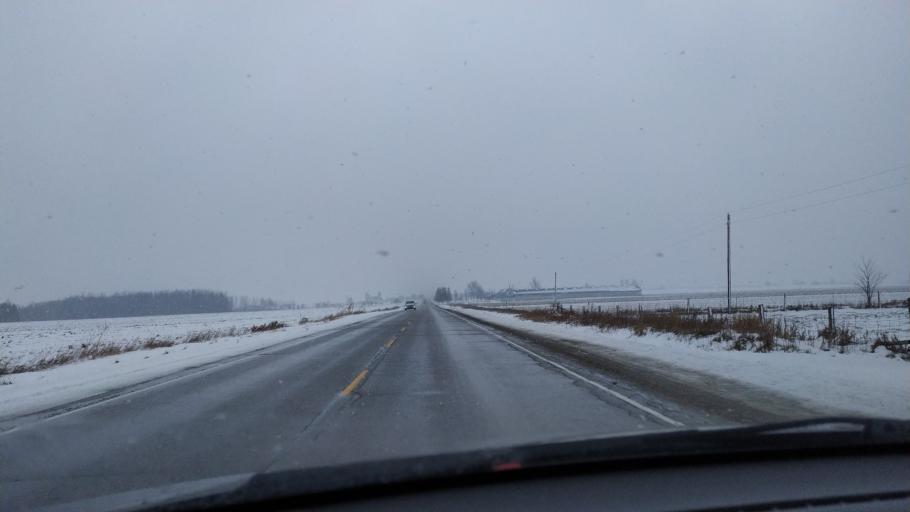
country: CA
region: Ontario
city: Stratford
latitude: 43.5143
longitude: -80.8839
